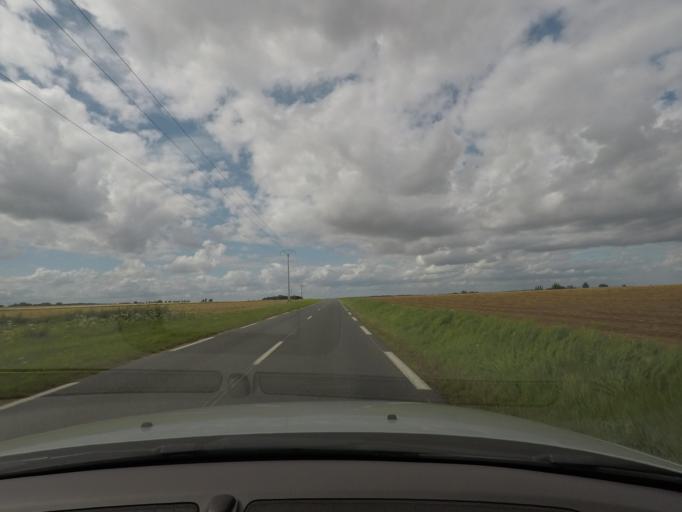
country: FR
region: Haute-Normandie
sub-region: Departement de l'Eure
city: Les Andelys
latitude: 49.2280
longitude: 1.4371
